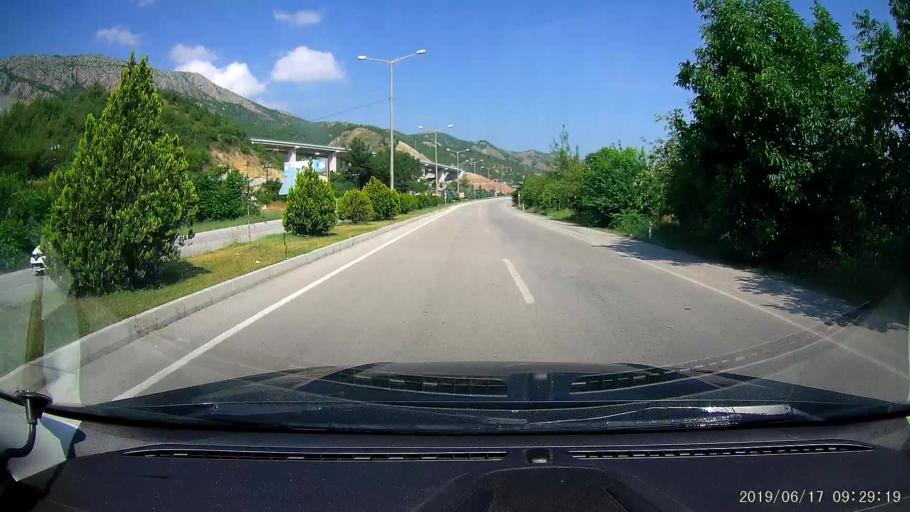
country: TR
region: Amasya
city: Amasya
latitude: 40.6958
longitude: 35.8135
